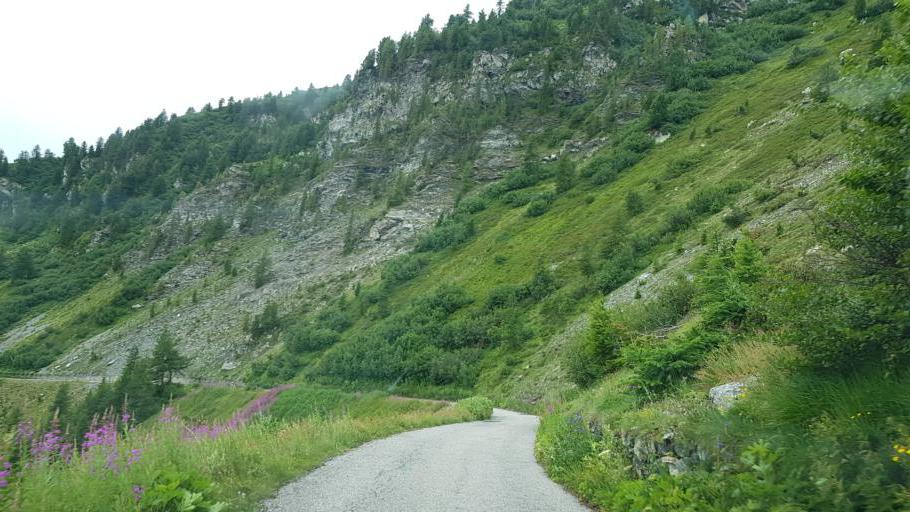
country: IT
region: Piedmont
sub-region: Provincia di Cuneo
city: Serre
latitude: 44.5498
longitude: 7.1267
